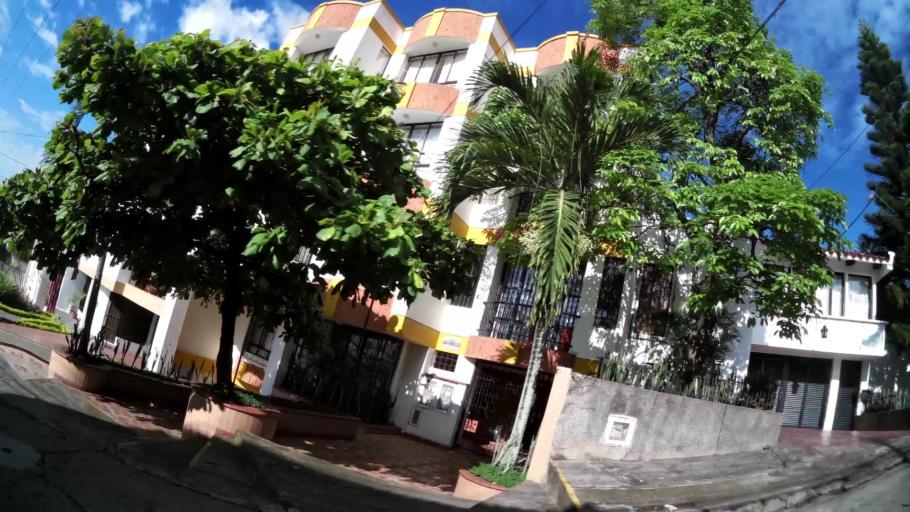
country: CO
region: Valle del Cauca
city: Cali
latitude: 3.4391
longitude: -76.5424
